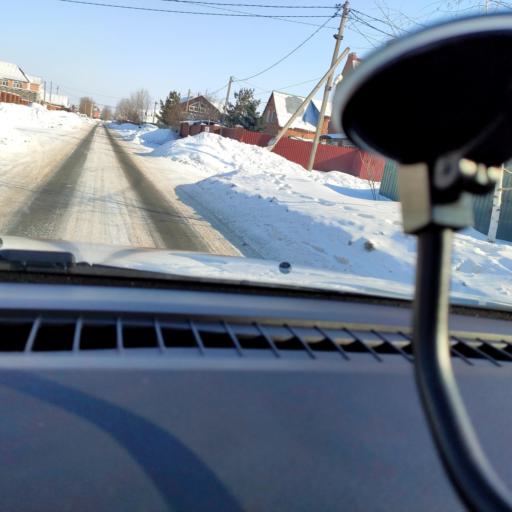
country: RU
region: Samara
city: Samara
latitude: 53.1353
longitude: 50.2400
